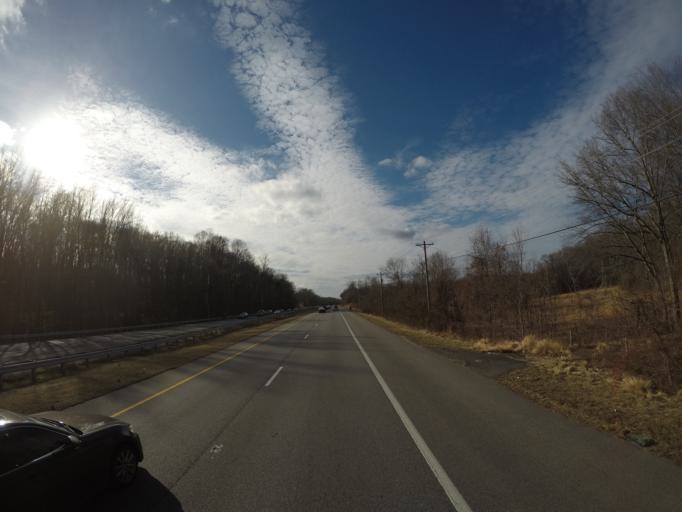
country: US
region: Maryland
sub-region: Charles County
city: Waldorf
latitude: 38.6525
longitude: -76.9799
